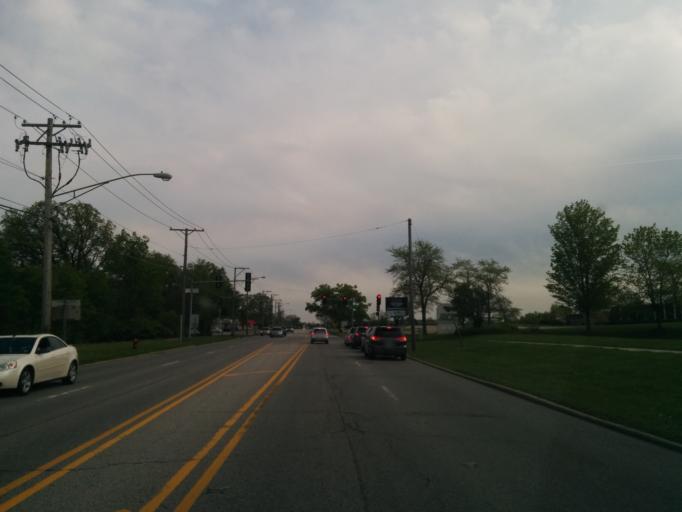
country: US
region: Illinois
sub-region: Kane County
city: North Aurora
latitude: 41.7993
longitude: -88.3250
